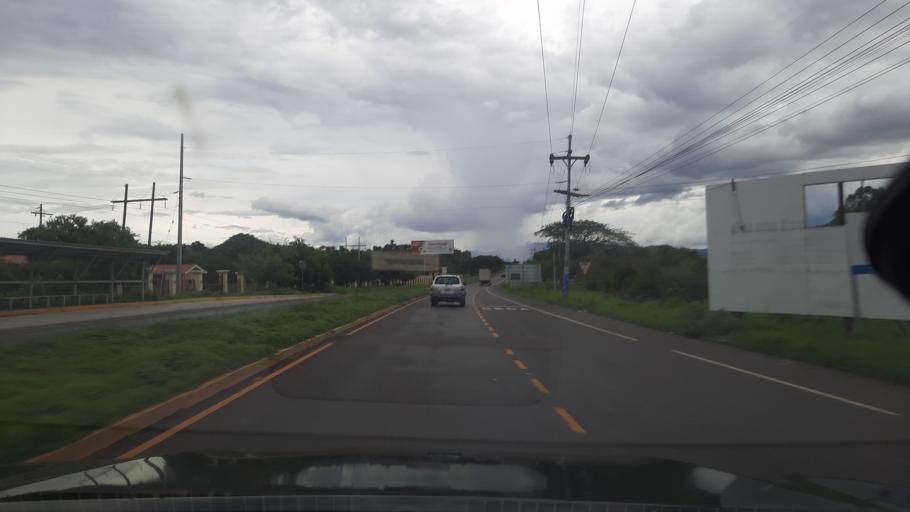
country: HN
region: Choluteca
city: Ciudad Choluteca
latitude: 13.3429
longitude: -87.2528
